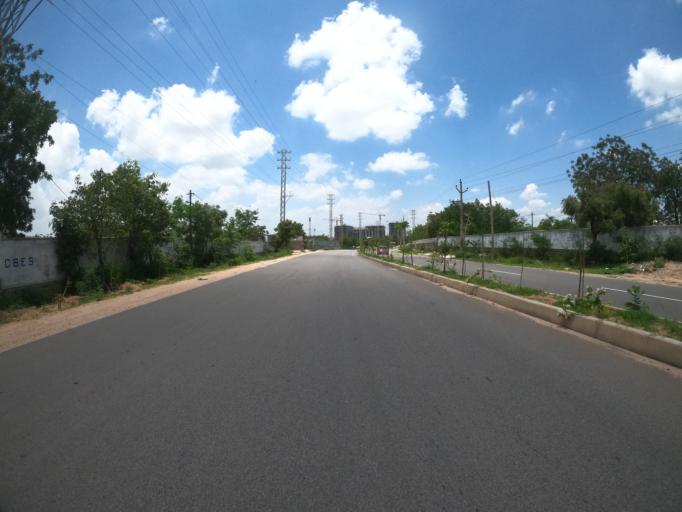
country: IN
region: Telangana
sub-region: Medak
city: Serilingampalle
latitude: 17.3950
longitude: 78.3177
